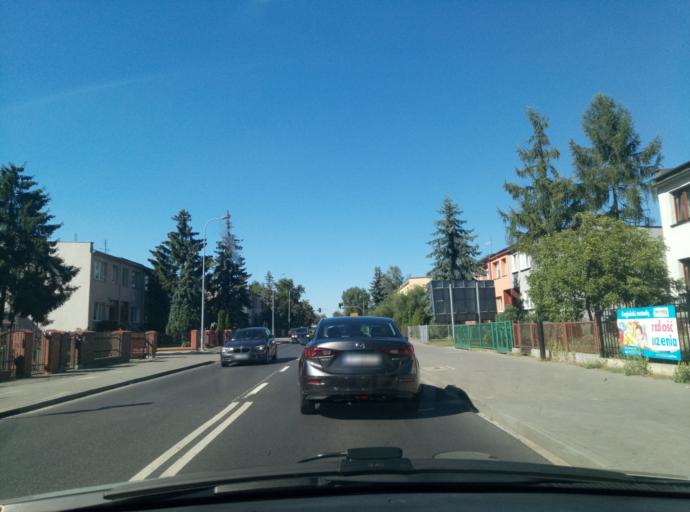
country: PL
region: Kujawsko-Pomorskie
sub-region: Torun
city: Torun
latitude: 53.0273
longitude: 18.6016
